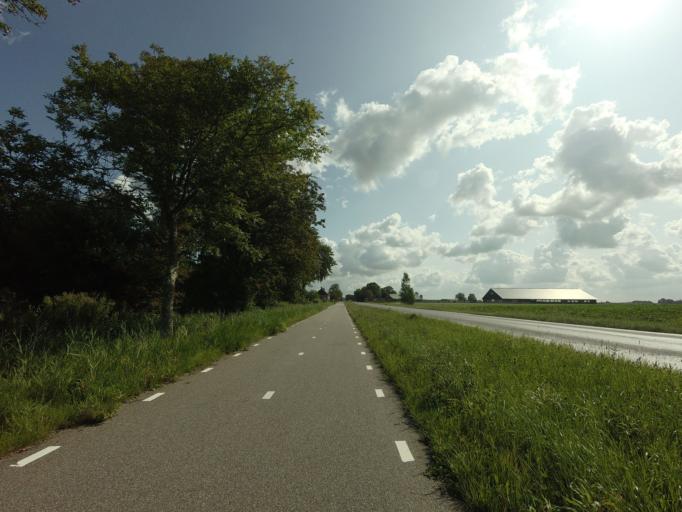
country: NL
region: Friesland
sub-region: Gemeente Het Bildt
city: Sint Jacobiparochie
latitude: 53.2737
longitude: 5.6170
